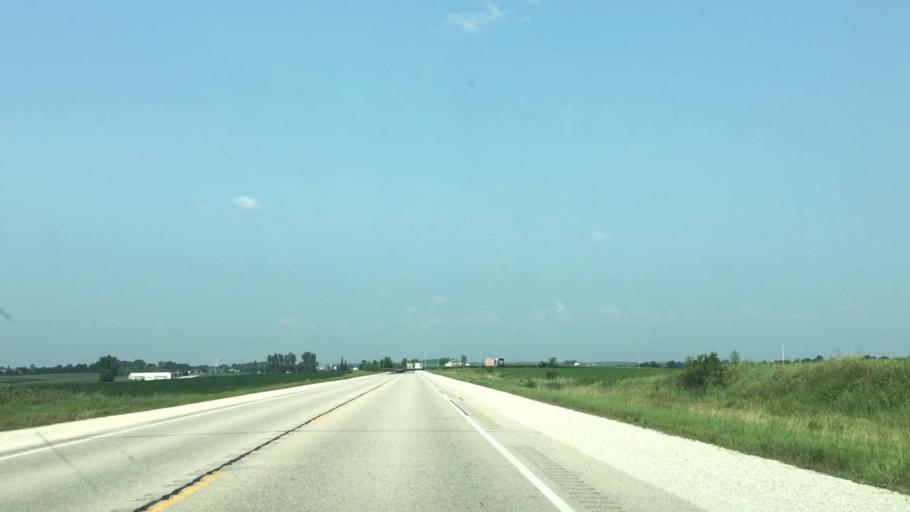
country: US
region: Iowa
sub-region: Winneshiek County
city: Decorah
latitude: 43.2501
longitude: -91.8415
